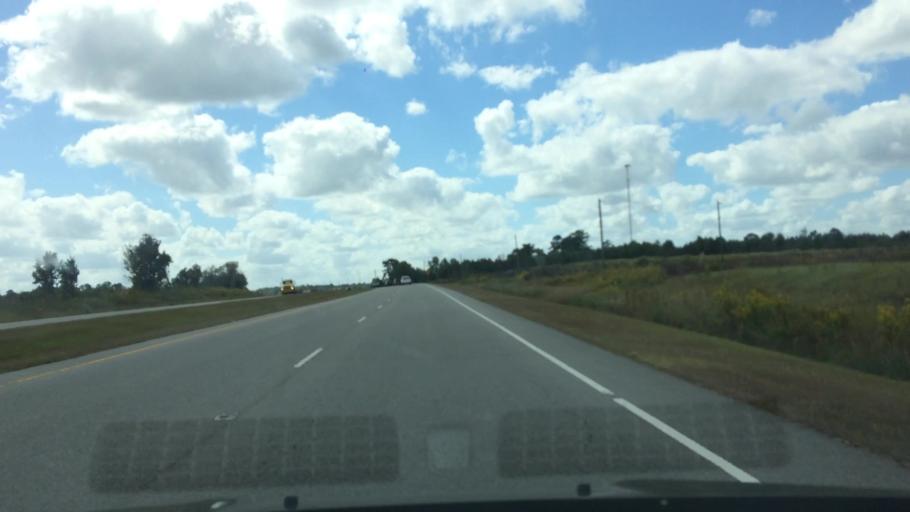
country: US
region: North Carolina
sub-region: Pitt County
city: Ayden
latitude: 35.4956
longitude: -77.4269
